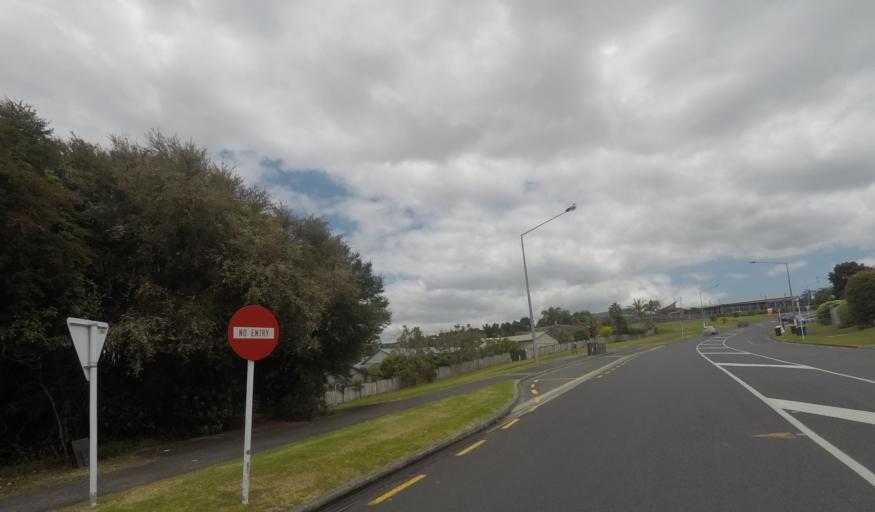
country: NZ
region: Auckland
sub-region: Auckland
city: Rosebank
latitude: -36.8234
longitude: 174.6105
